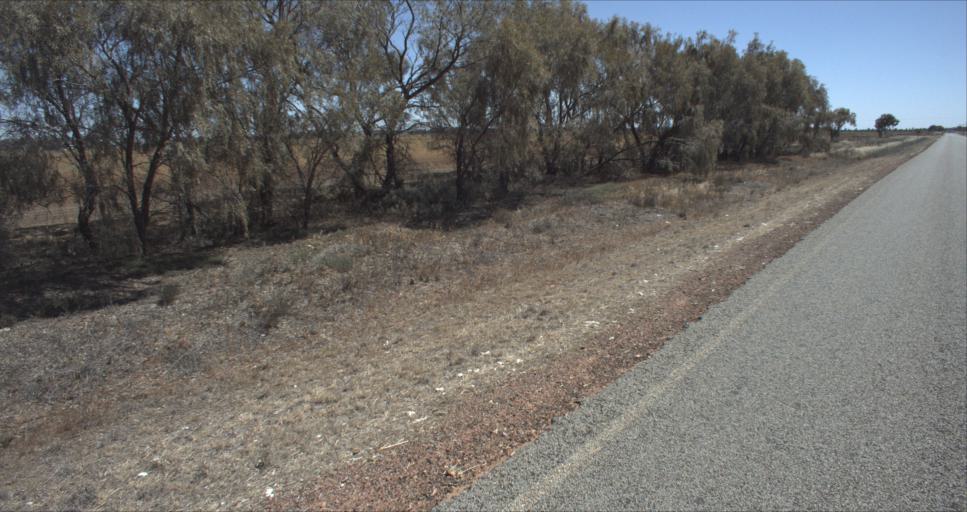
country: AU
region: New South Wales
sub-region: Leeton
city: Leeton
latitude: -34.4603
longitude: 146.2943
